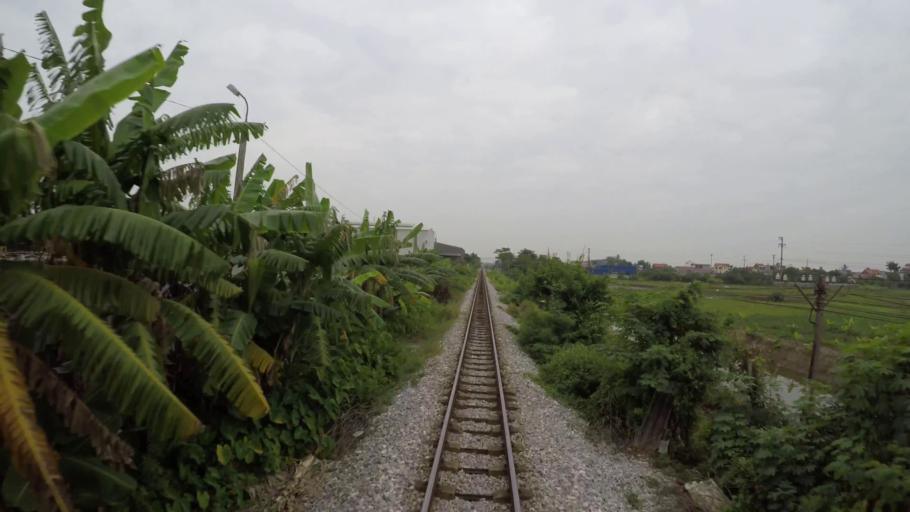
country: VN
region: Hai Phong
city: An Duong
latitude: 20.8928
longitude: 106.5905
